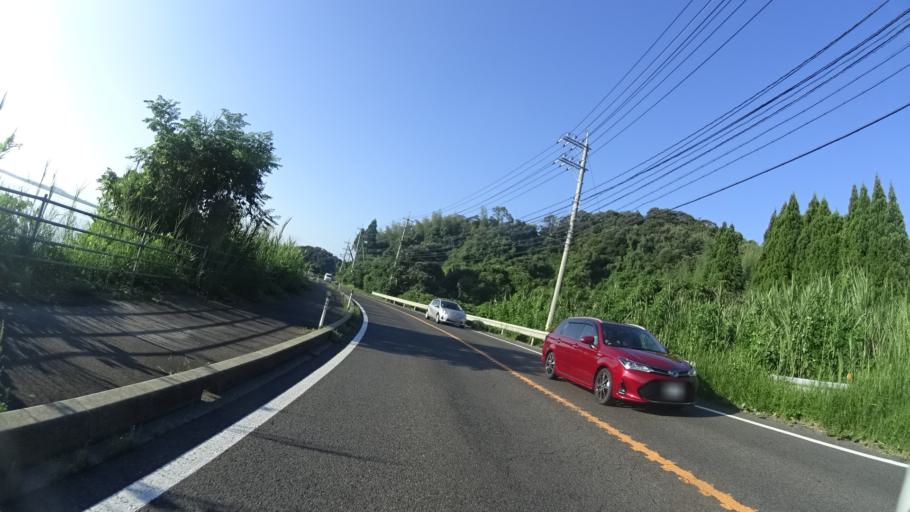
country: JP
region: Shimane
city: Sakaiminato
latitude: 35.5256
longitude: 133.1486
